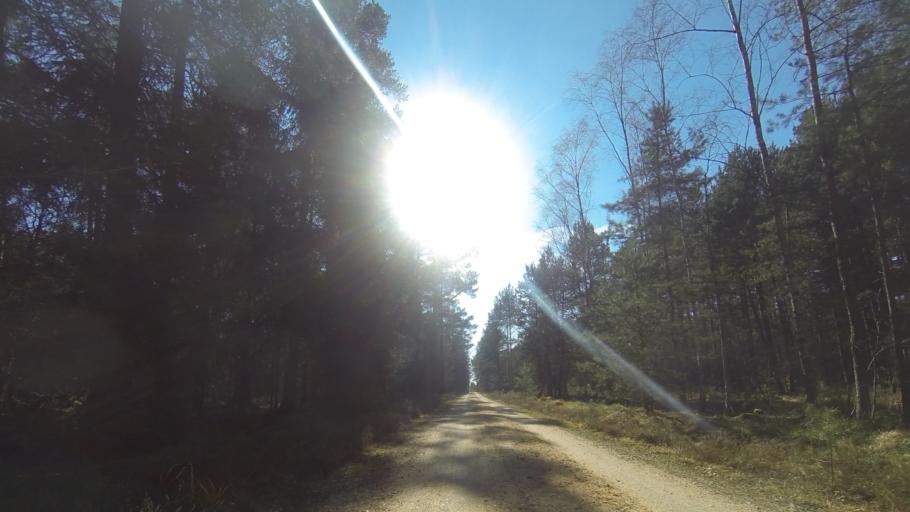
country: DE
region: Saxony
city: Laussnitz
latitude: 51.2517
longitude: 13.8423
